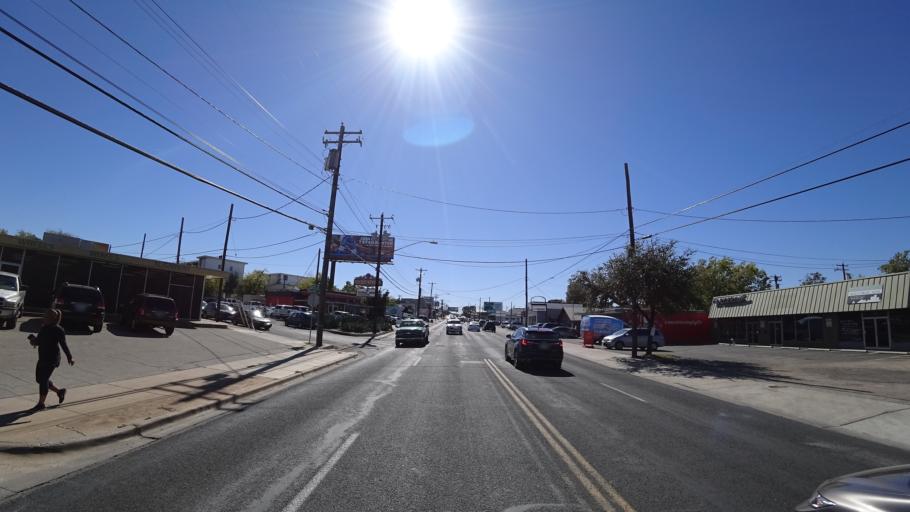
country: US
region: Texas
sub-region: Travis County
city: Austin
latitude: 30.3239
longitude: -97.7395
